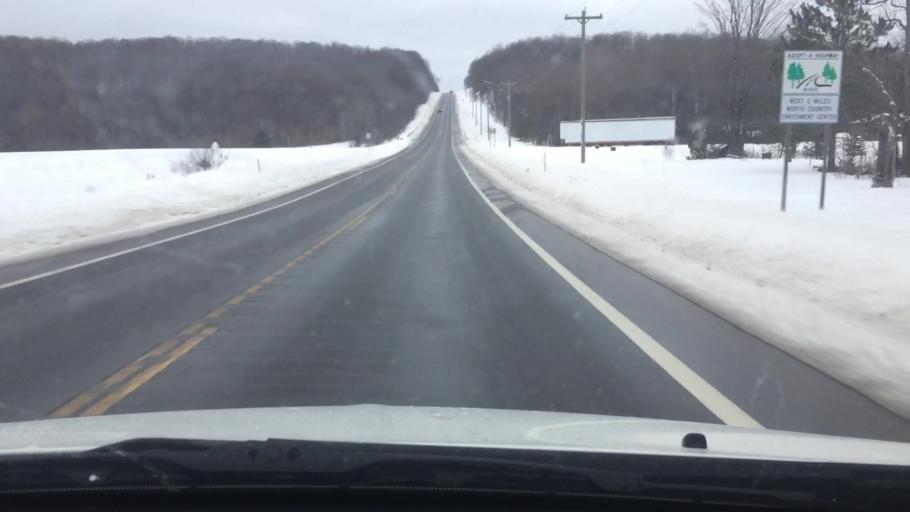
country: US
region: Michigan
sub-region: Charlevoix County
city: Boyne City
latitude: 45.0964
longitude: -85.0004
